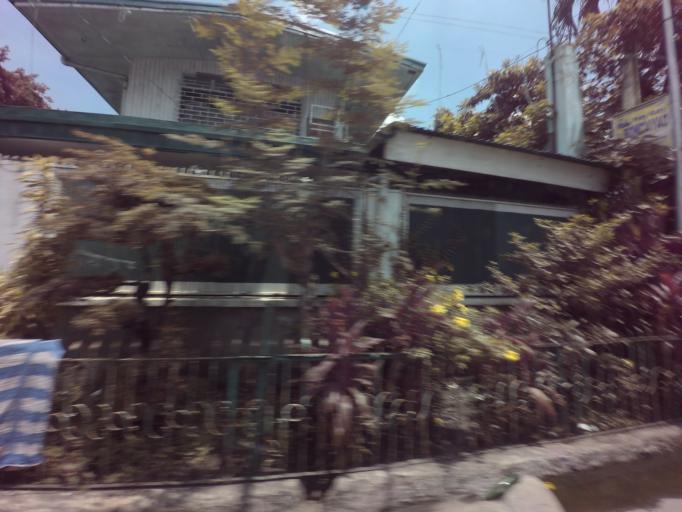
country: PH
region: Calabarzon
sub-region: Province of Laguna
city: San Pedro
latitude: 14.3899
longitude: 121.0468
